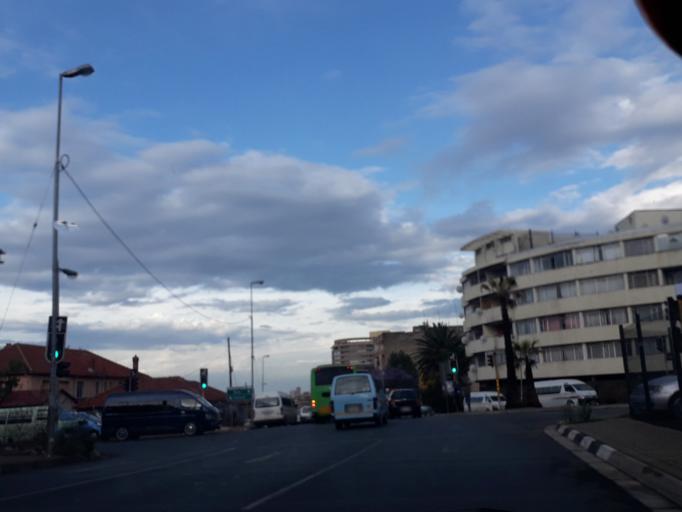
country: ZA
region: Gauteng
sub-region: City of Johannesburg Metropolitan Municipality
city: Johannesburg
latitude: -26.1820
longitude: 28.0487
